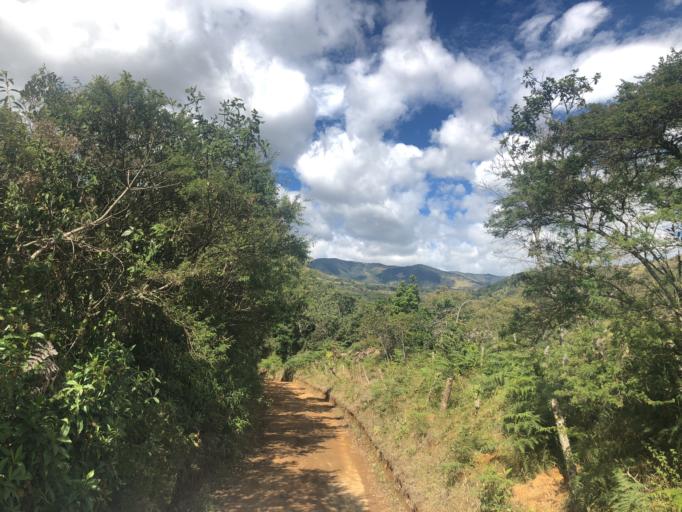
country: CO
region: Cauca
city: Silvia
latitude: 2.6826
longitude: -76.4377
